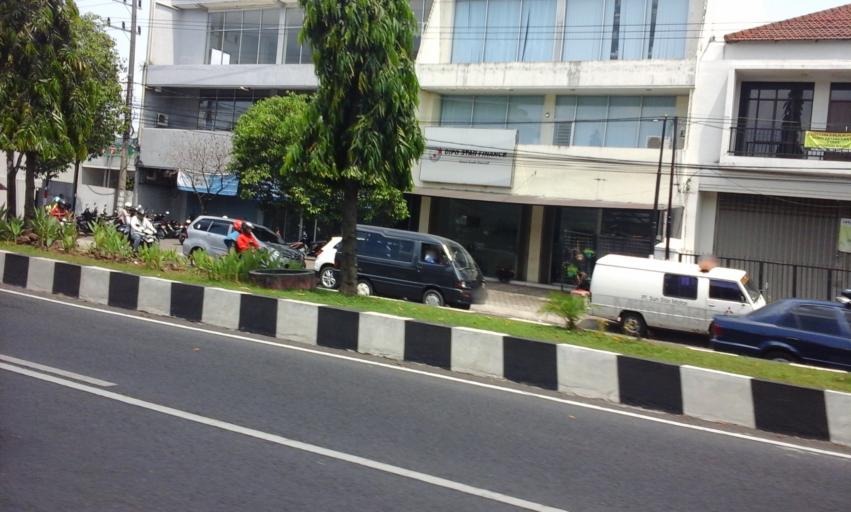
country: ID
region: East Java
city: Kaliwates
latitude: -8.1787
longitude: 113.6787
